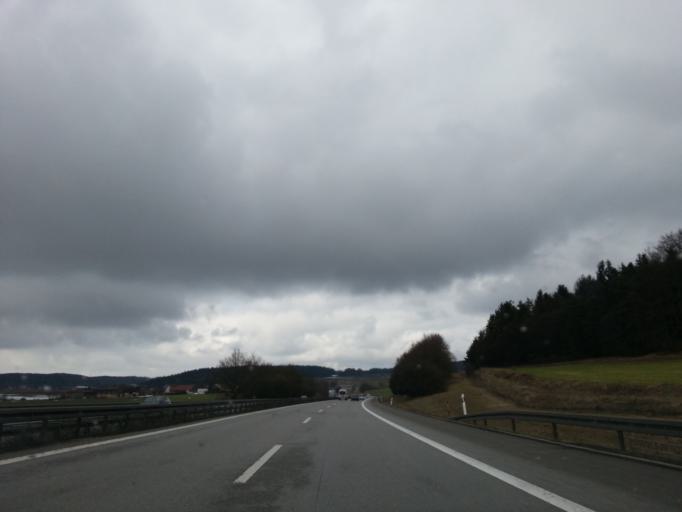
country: DE
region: Bavaria
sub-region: Upper Palatinate
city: Hohenfels
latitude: 49.1551
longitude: 11.8417
